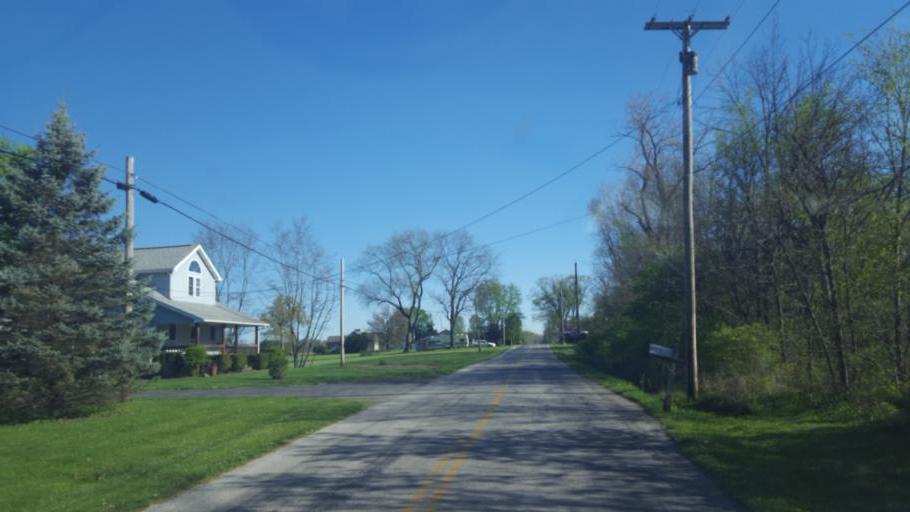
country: US
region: Ohio
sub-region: Morrow County
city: Cardington
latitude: 40.6431
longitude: -82.9657
